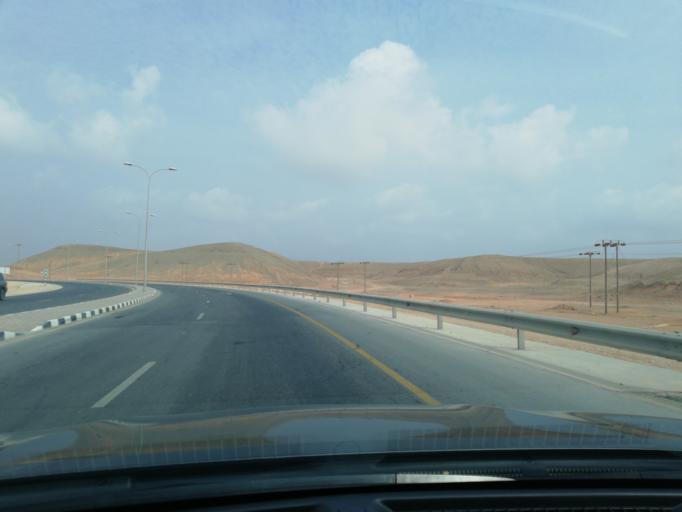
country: OM
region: Zufar
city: Salalah
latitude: 16.9499
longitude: 53.9862
